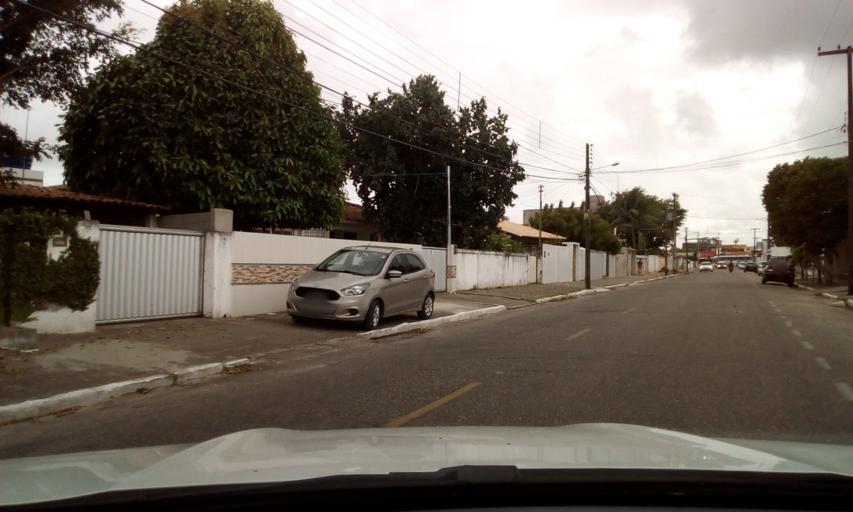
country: BR
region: Paraiba
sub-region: Joao Pessoa
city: Joao Pessoa
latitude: -7.1613
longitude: -34.8676
